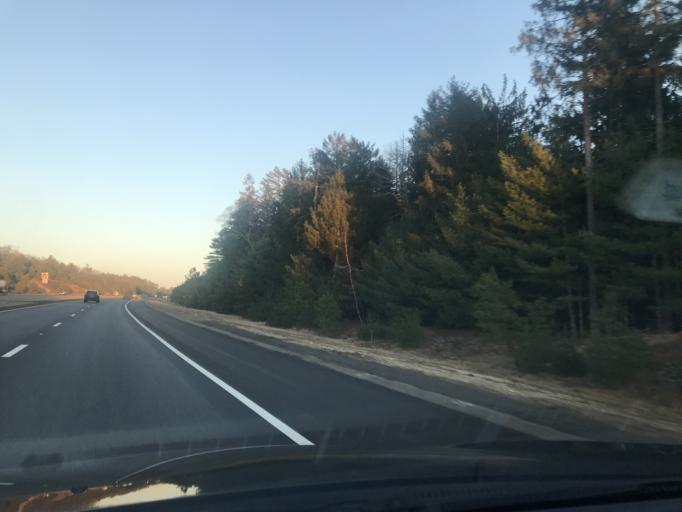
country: US
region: Massachusetts
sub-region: Plymouth County
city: Kingston
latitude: 41.9588
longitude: -70.7516
